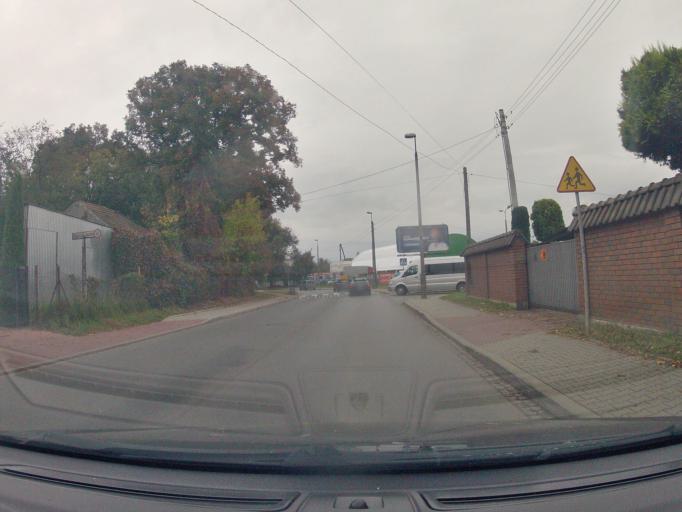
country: PL
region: Lesser Poland Voivodeship
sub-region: Powiat krakowski
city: Rzaska
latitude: 50.0767
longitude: 19.8816
